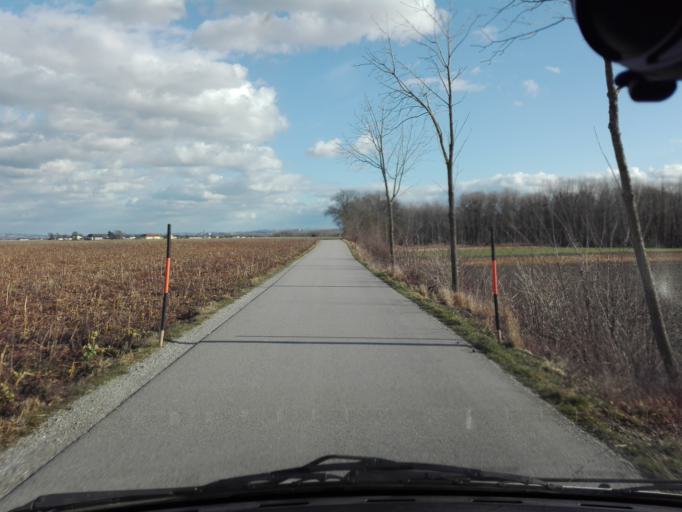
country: AT
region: Lower Austria
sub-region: Politischer Bezirk Amstetten
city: Strengberg
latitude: 48.1915
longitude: 14.6378
